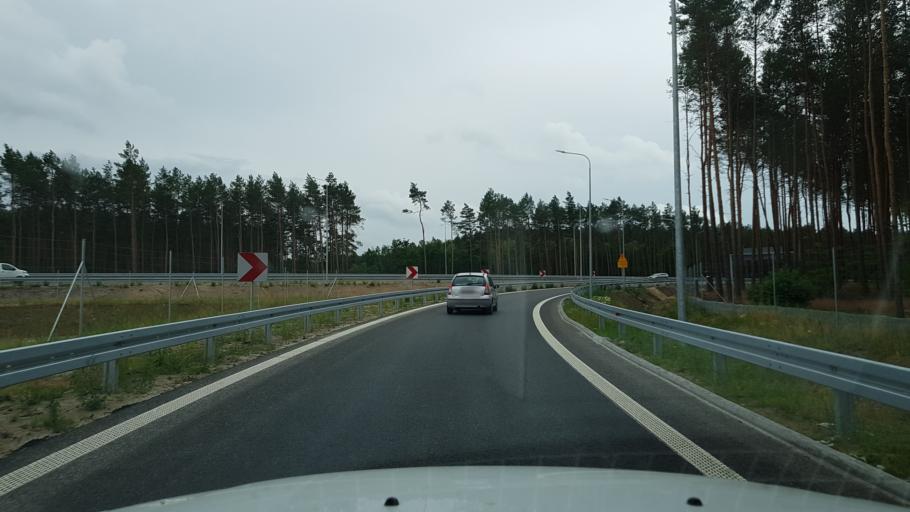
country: PL
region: West Pomeranian Voivodeship
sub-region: Powiat stargardzki
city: Kobylanka
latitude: 53.4250
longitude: 14.7673
